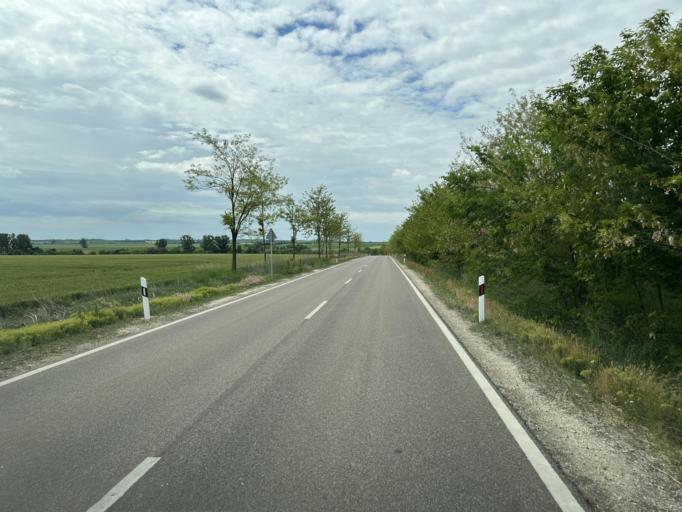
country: HU
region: Pest
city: Zsambok
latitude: 47.5275
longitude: 19.6006
